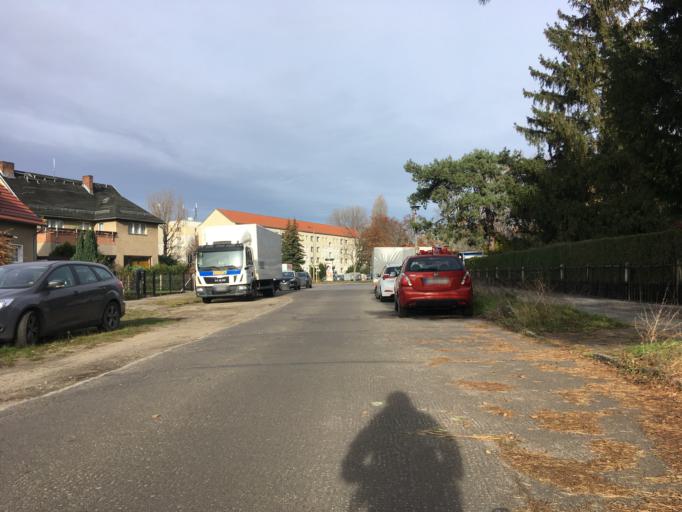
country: DE
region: Berlin
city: Adlershof
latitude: 52.4502
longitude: 13.5394
